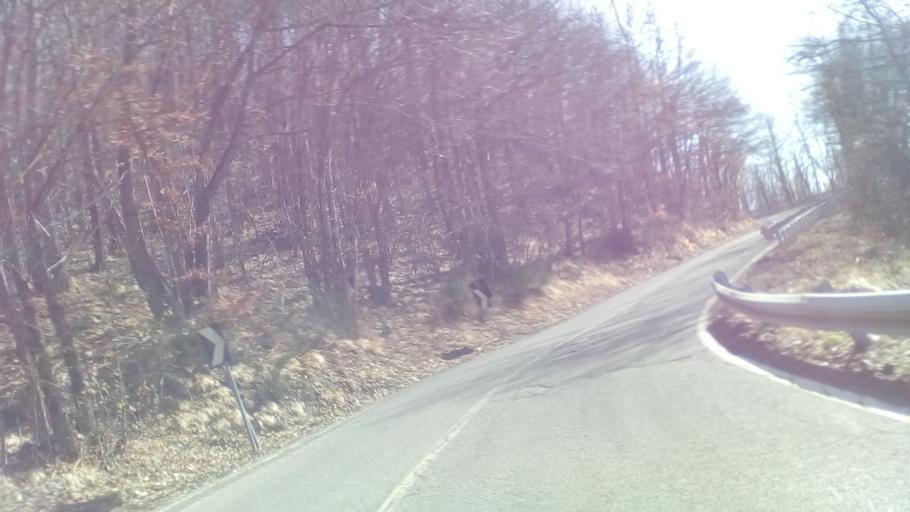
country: IT
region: Emilia-Romagna
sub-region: Provincia di Modena
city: Pievepelago
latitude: 44.2163
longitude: 10.6177
